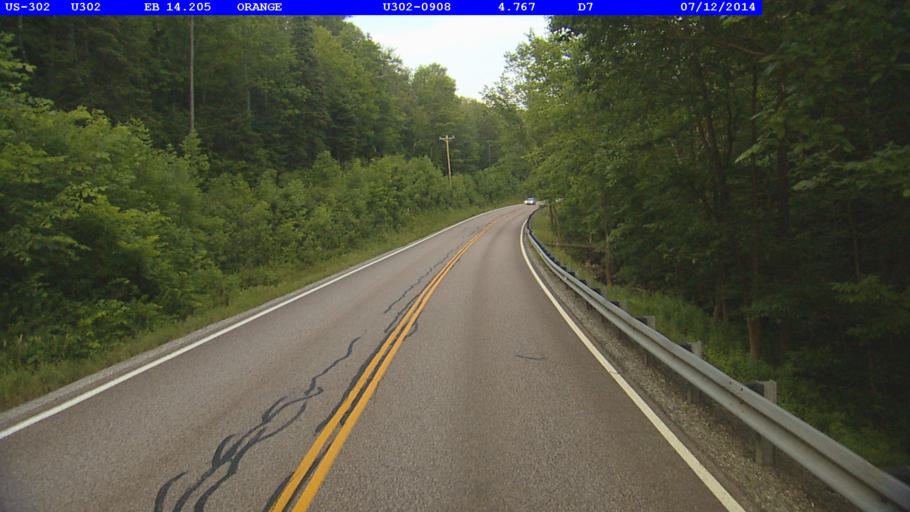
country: US
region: Vermont
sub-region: Washington County
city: South Barre
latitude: 44.1428
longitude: -72.3457
